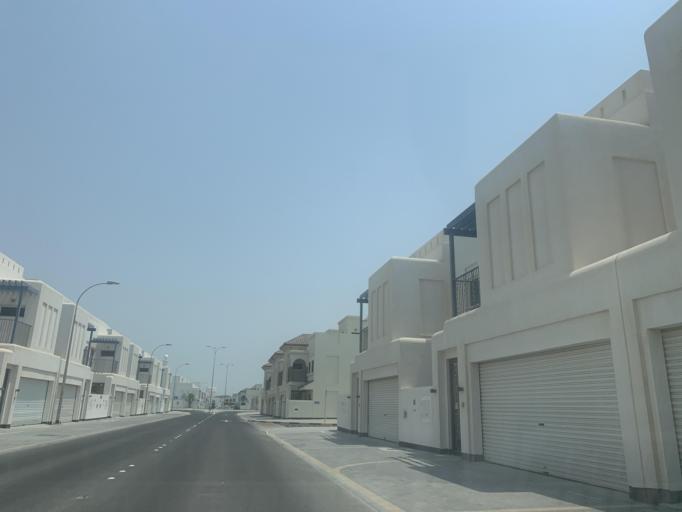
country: BH
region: Muharraq
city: Al Muharraq
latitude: 26.3133
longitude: 50.6234
